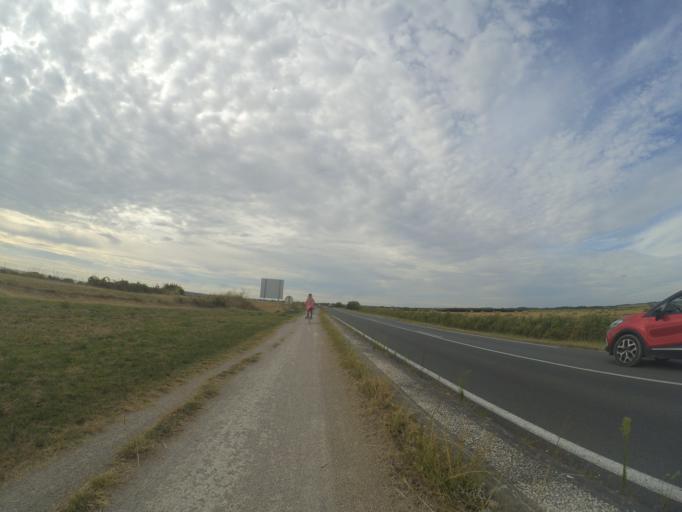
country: FR
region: Poitou-Charentes
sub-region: Departement de la Charente-Maritime
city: Meschers-sur-Gironde
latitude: 45.5393
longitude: -0.9064
